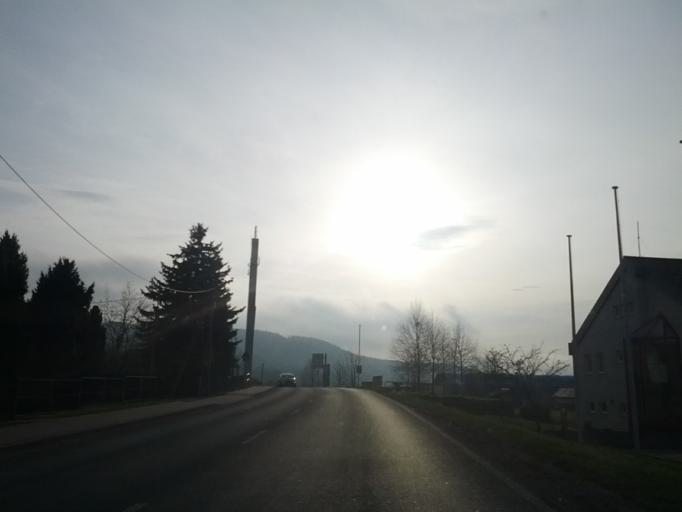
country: DE
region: Thuringia
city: Wasungen
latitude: 50.6576
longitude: 10.3736
